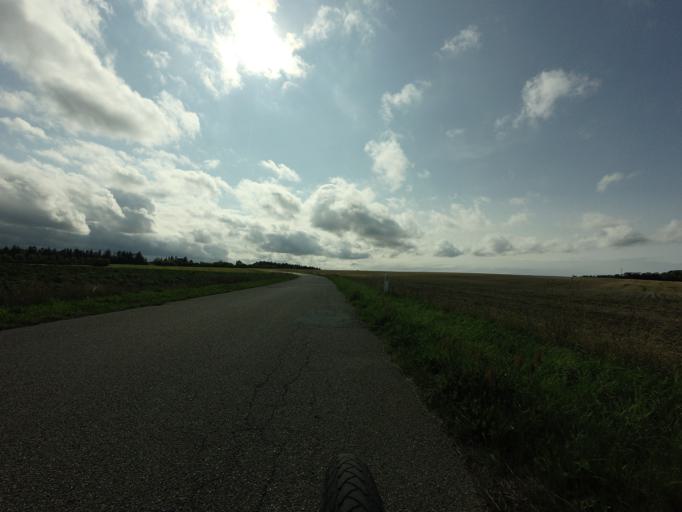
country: DK
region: North Denmark
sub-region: Hjorring Kommune
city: Hirtshals
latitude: 57.5497
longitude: 10.0583
